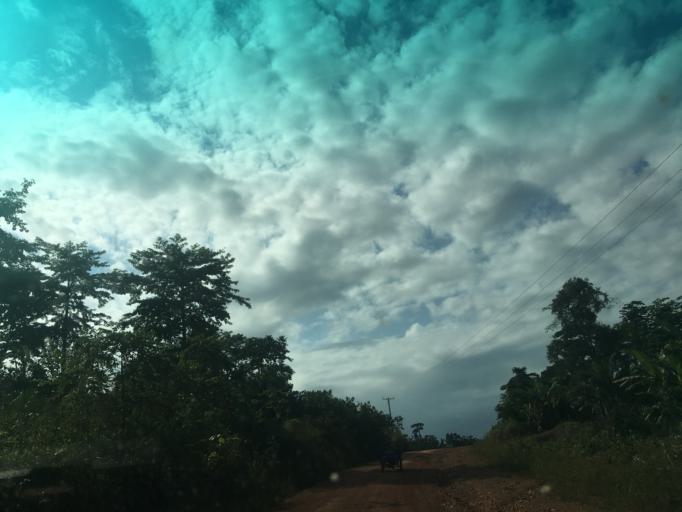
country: GH
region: Western
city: Wassa-Akropong
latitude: 5.9140
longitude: -2.4054
